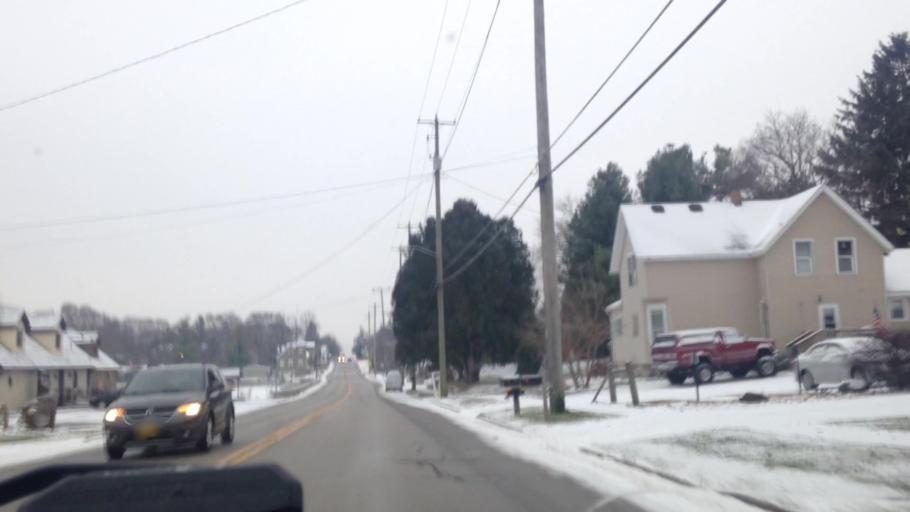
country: US
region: Wisconsin
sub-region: Dodge County
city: Hustisford
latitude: 43.3140
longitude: -88.5184
